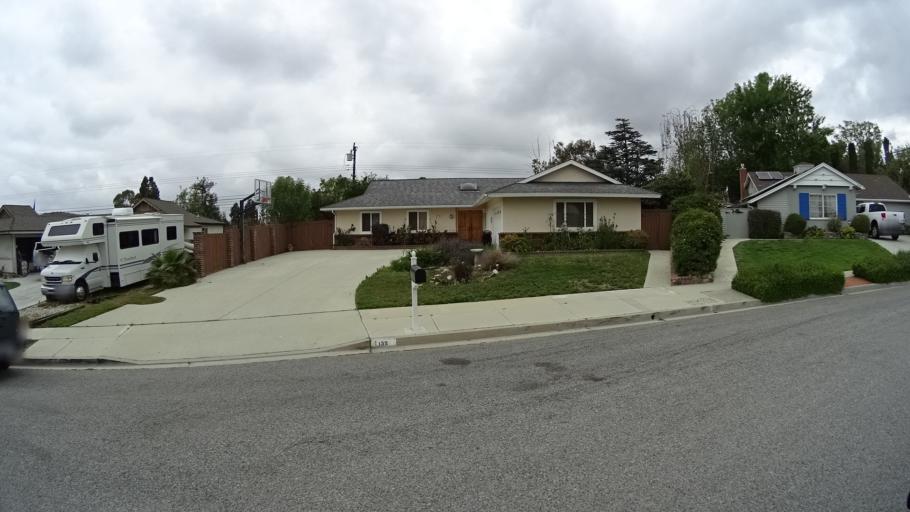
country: US
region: California
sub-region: Ventura County
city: Thousand Oaks
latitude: 34.2144
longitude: -118.8790
